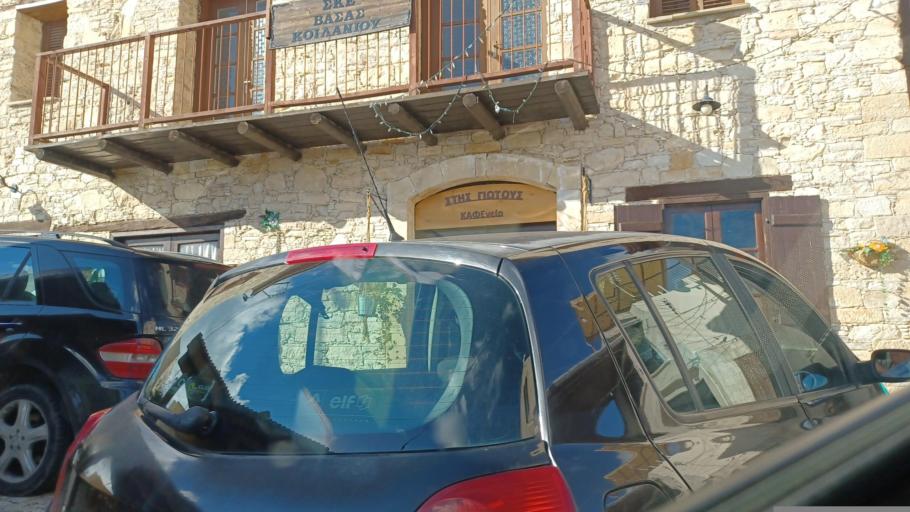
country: CY
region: Limassol
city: Pachna
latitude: 34.8337
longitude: 32.7923
